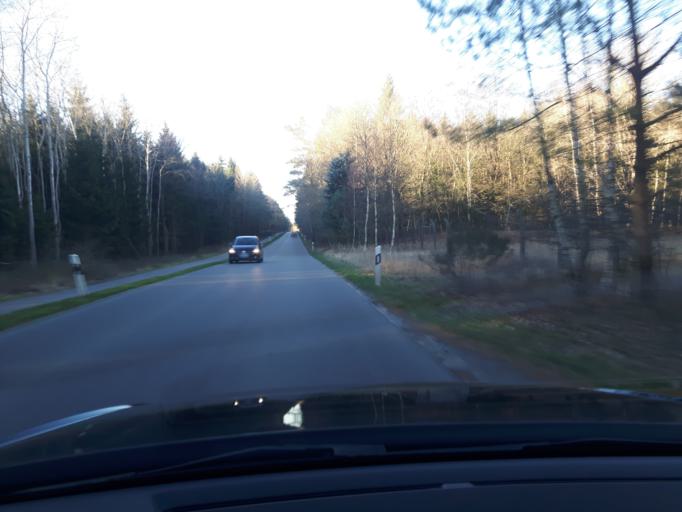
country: DE
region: Mecklenburg-Vorpommern
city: Sehlen
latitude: 54.3795
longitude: 13.3996
